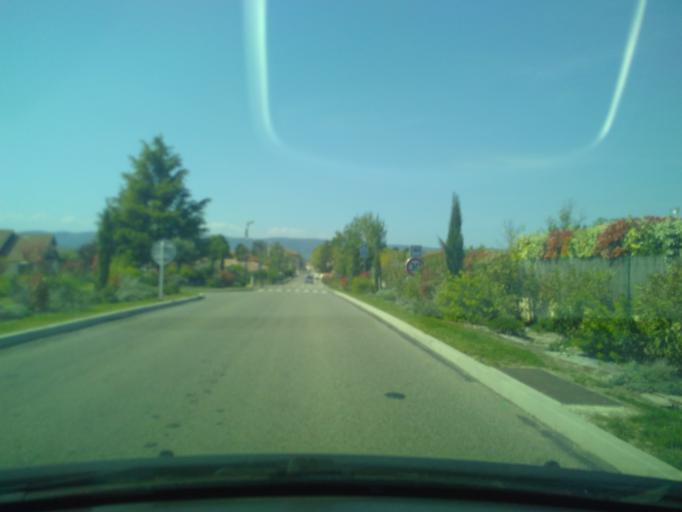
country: FR
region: Rhone-Alpes
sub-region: Departement de la Drome
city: La Begude-de-Mazenc
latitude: 44.5899
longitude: 4.9551
